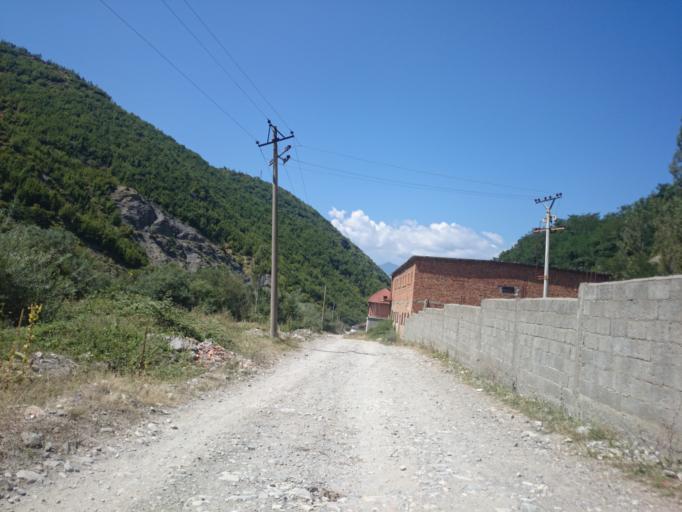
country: AL
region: Diber
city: Peshkopi
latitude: 41.6853
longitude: 20.4549
